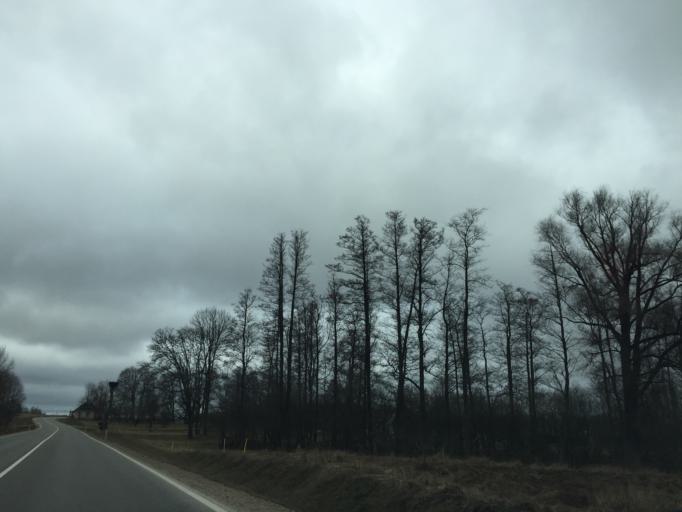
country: LV
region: Ilukste
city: Ilukste
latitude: 55.9995
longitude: 26.2831
